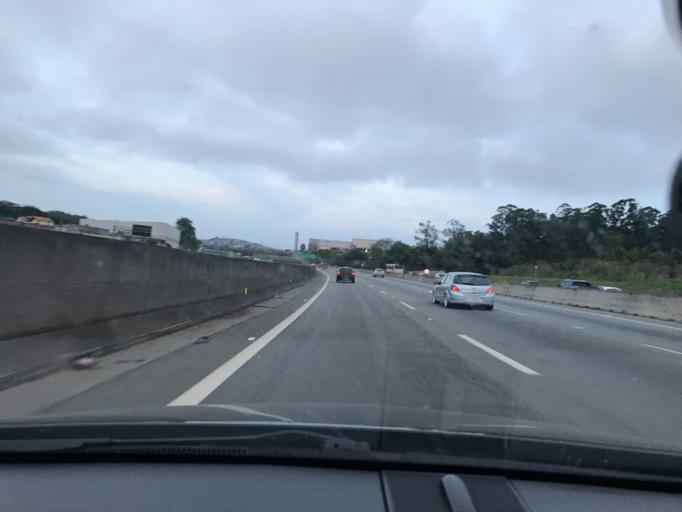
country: BR
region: Sao Paulo
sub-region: Itaquaquecetuba
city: Itaquaquecetuba
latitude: -23.4776
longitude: -46.4397
